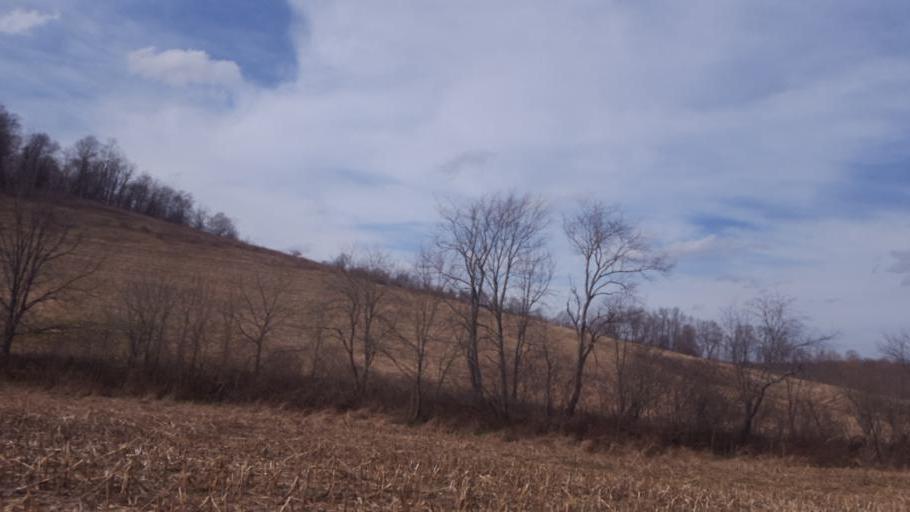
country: US
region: Ohio
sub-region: Sandusky County
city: Bellville
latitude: 40.5617
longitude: -82.4020
